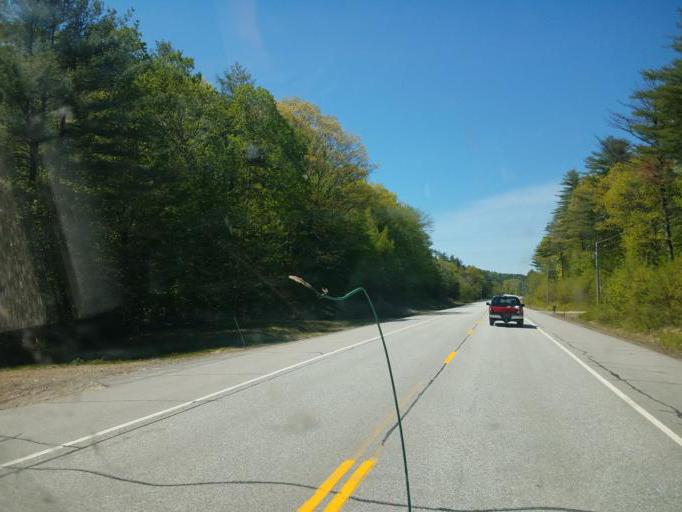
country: US
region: New Hampshire
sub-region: Grafton County
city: Rumney
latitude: 43.8088
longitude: -71.8632
